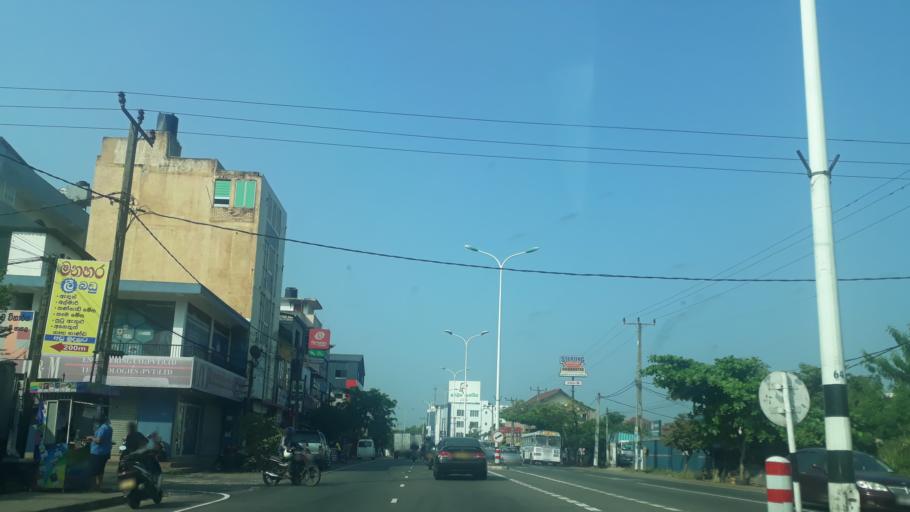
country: LK
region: Western
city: Kelaniya
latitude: 6.9947
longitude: 79.9456
